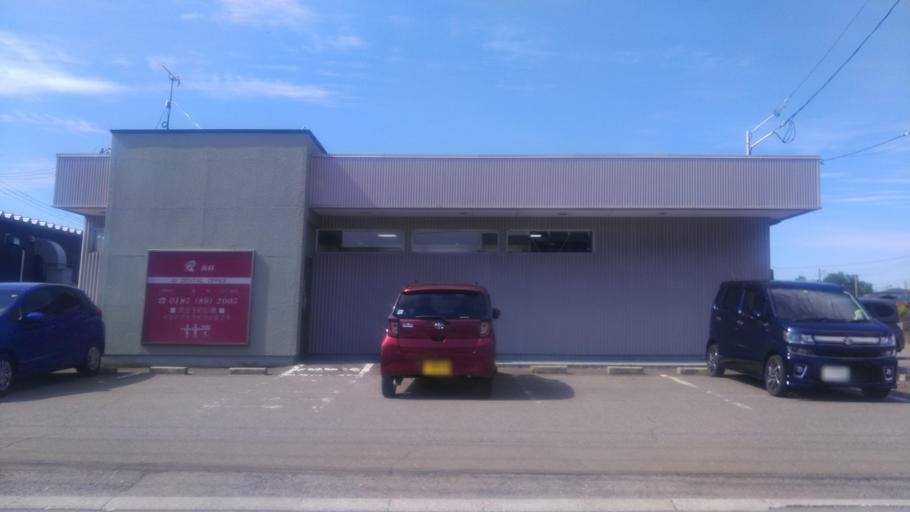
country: JP
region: Akita
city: Noshiromachi
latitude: 40.1914
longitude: 140.0227
